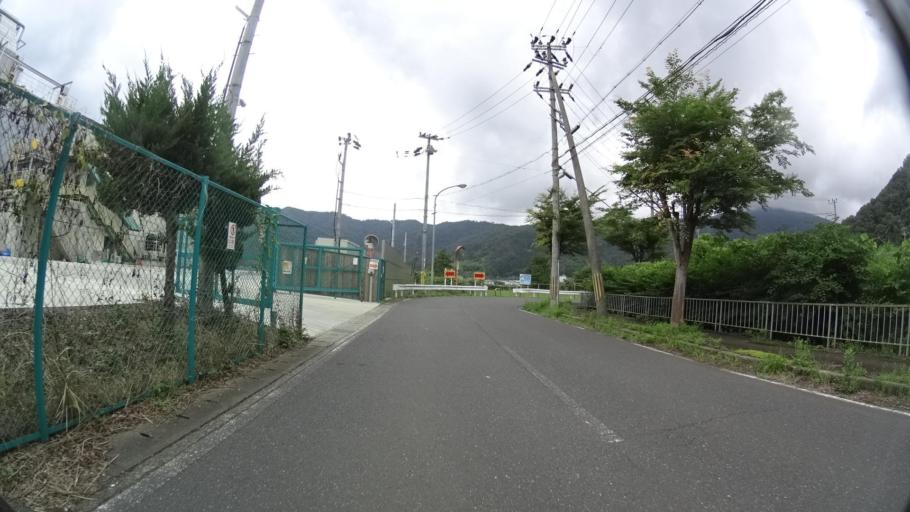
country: JP
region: Kyoto
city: Maizuru
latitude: 35.5055
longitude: 135.3799
